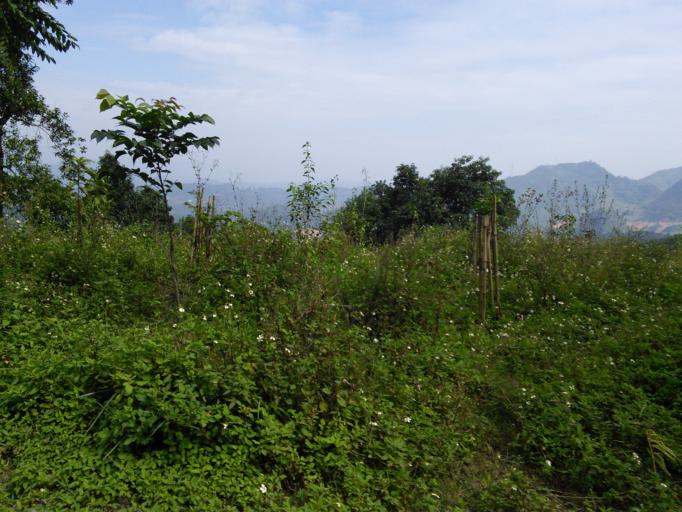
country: VN
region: Lao Cai
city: Lao Cai
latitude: 22.4499
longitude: 103.9348
